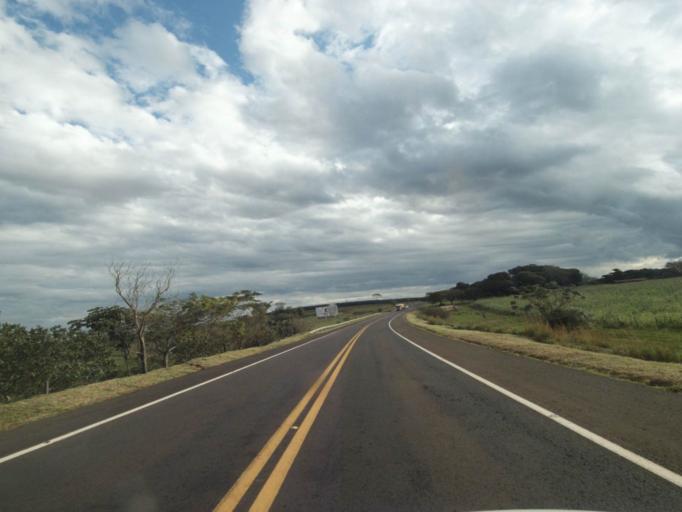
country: PY
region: Canindeyu
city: Salto del Guaira
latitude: -24.0828
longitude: -54.0686
